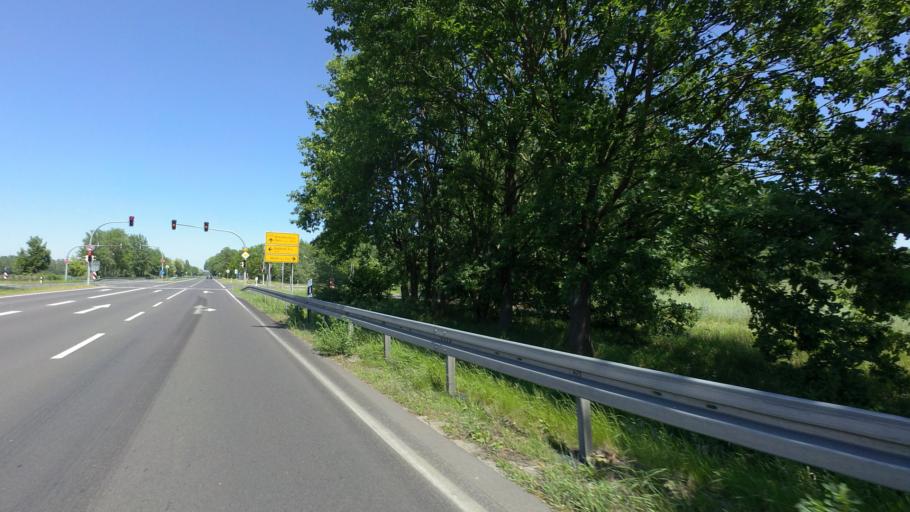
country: DE
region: Brandenburg
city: Peitz
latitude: 51.8254
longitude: 14.3869
